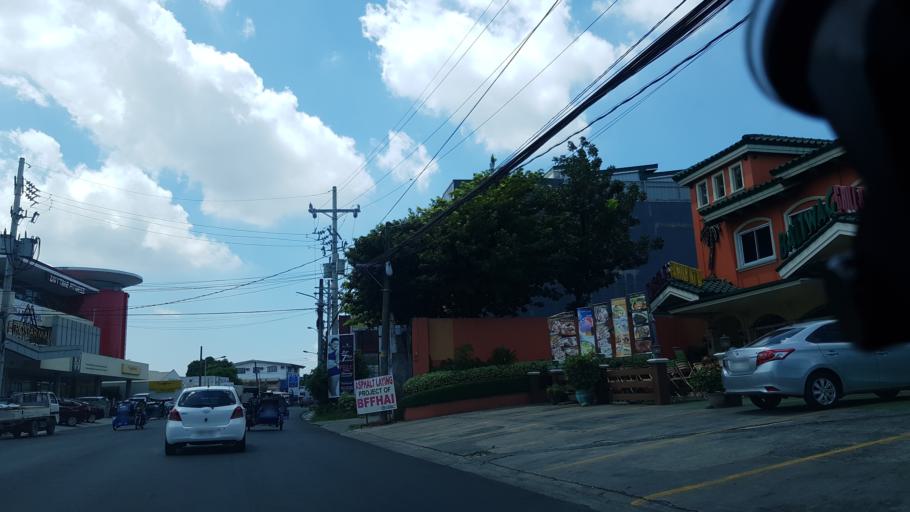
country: PH
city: Sambayanihan People's Village
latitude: 14.4457
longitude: 121.0220
